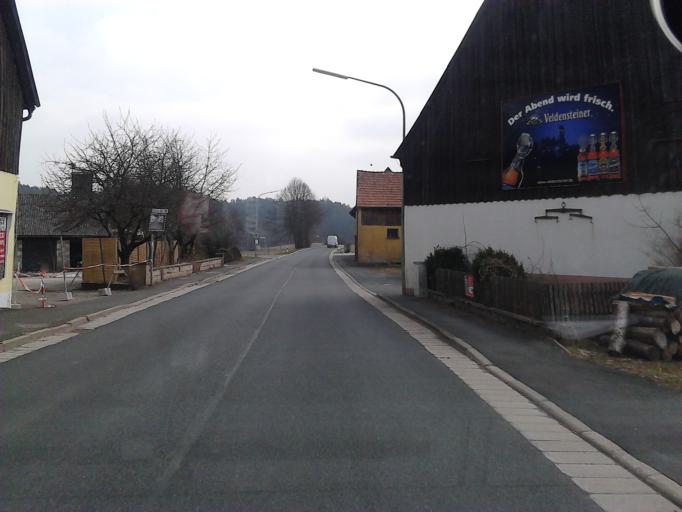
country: DE
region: Bavaria
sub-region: Regierungsbezirk Mittelfranken
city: Velden
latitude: 49.6419
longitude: 11.5110
